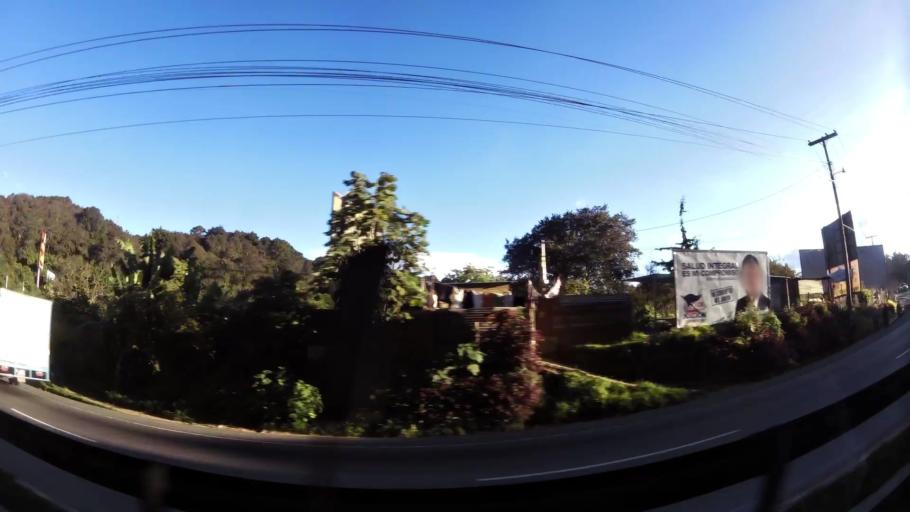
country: GT
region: Sacatepequez
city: San Lucas Sacatepequez
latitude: 14.6126
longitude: -90.6515
